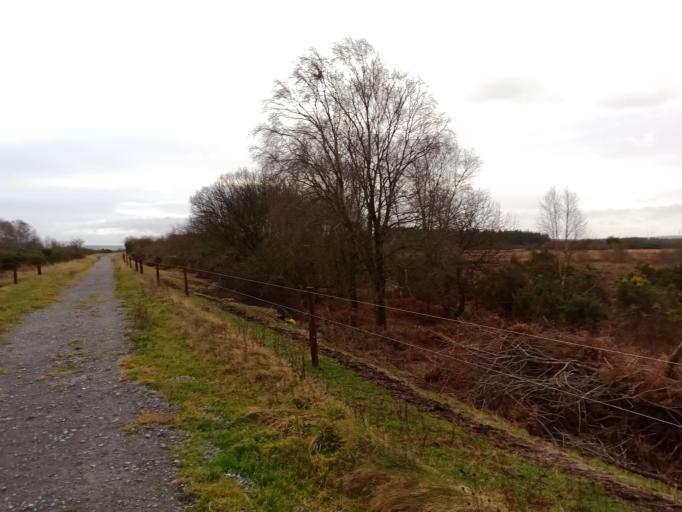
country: IE
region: Munster
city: Thurles
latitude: 52.6016
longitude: -7.7525
